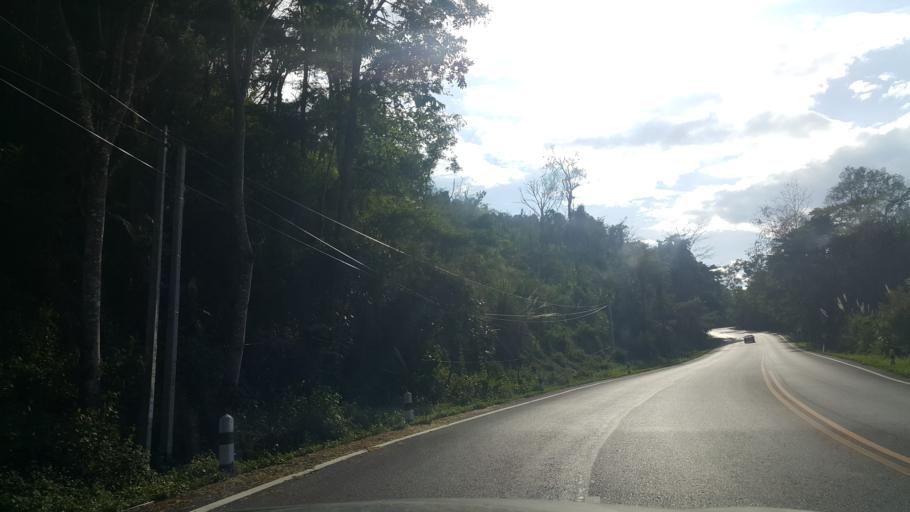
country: TH
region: Phayao
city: Phayao
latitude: 19.0600
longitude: 99.7987
